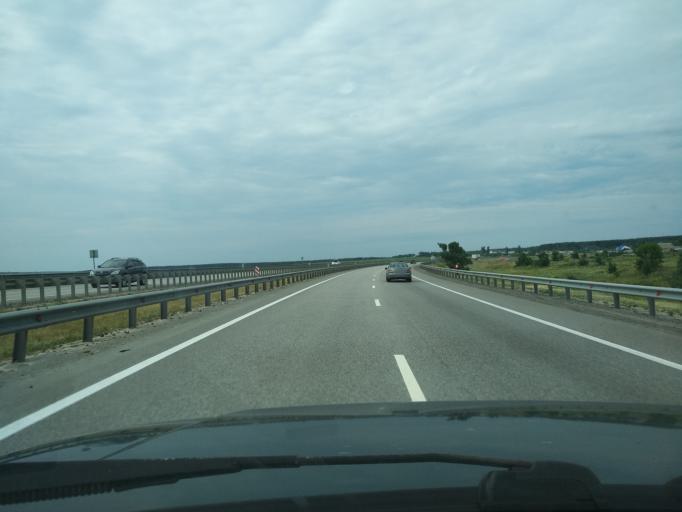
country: RU
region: Lipetsk
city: Khlevnoye
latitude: 52.0652
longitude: 39.1798
